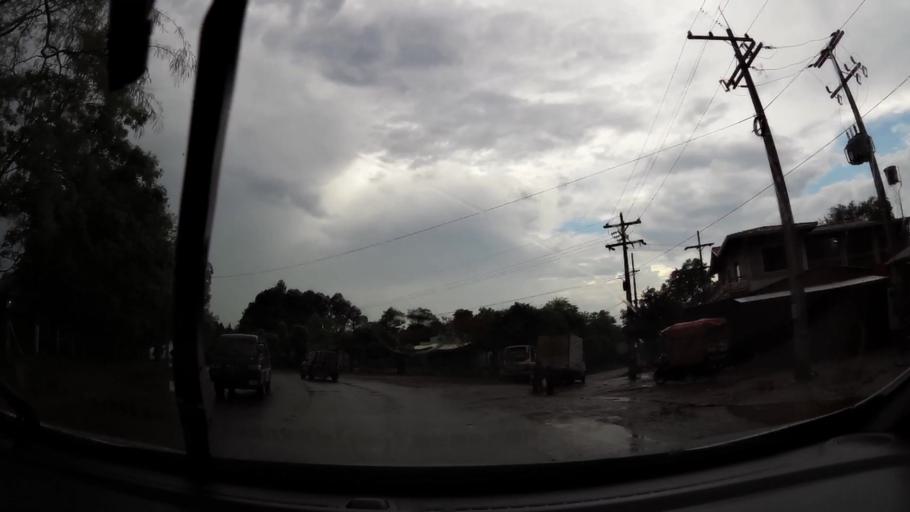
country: PY
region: Alto Parana
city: Presidente Franco
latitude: -25.5698
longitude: -54.6711
